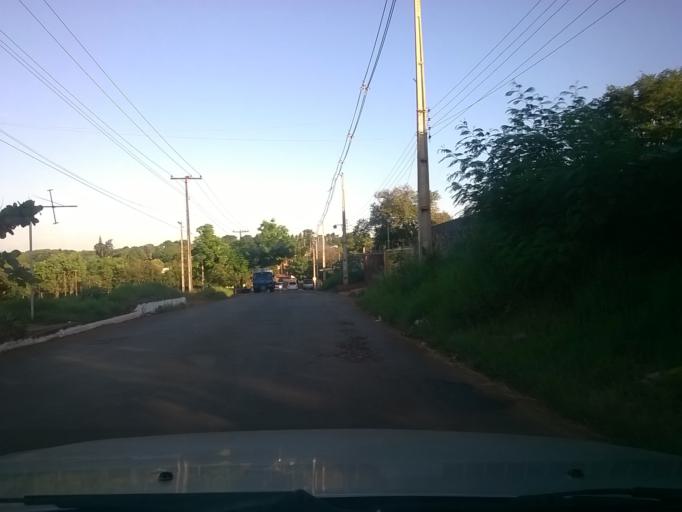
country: PY
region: Alto Parana
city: Presidente Franco
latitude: -25.5338
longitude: -54.6471
